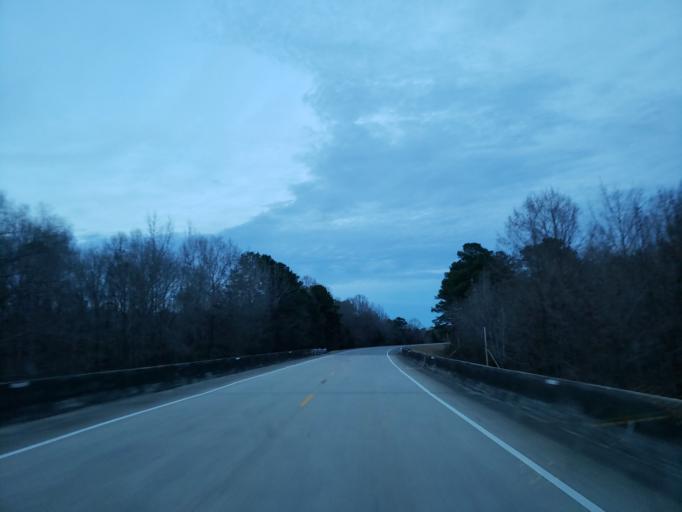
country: US
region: Alabama
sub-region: Sumter County
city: Livingston
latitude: 32.8319
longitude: -88.1517
